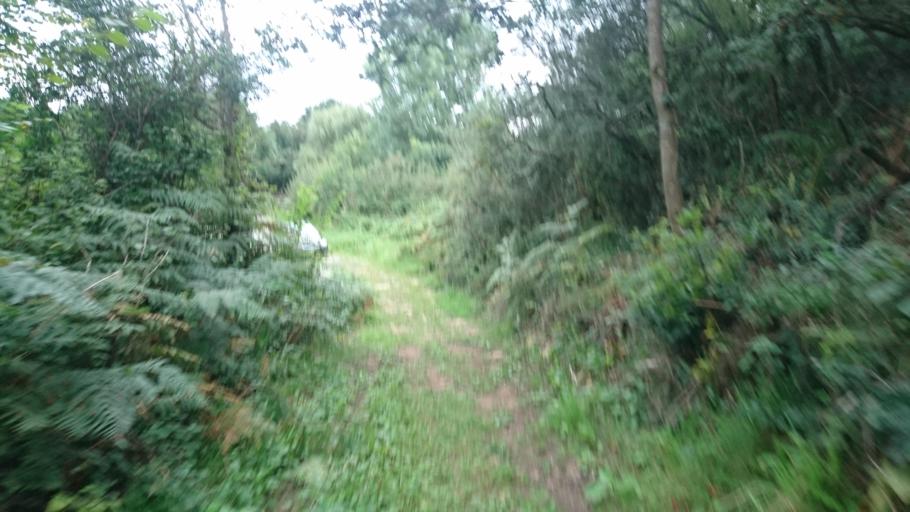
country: FR
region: Brittany
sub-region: Departement du Finistere
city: Lampaul-Plouarzel
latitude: 48.4426
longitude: -4.7561
